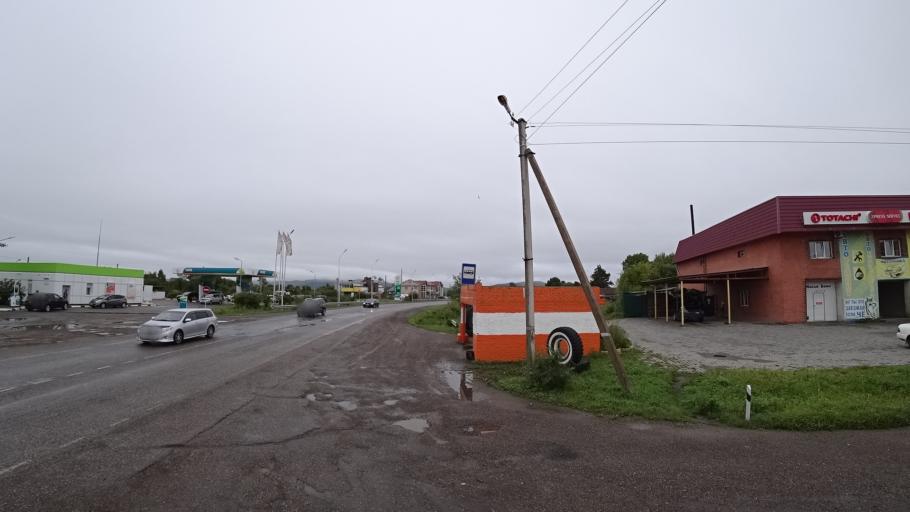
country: RU
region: Primorskiy
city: Monastyrishche
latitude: 44.2030
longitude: 132.4503
